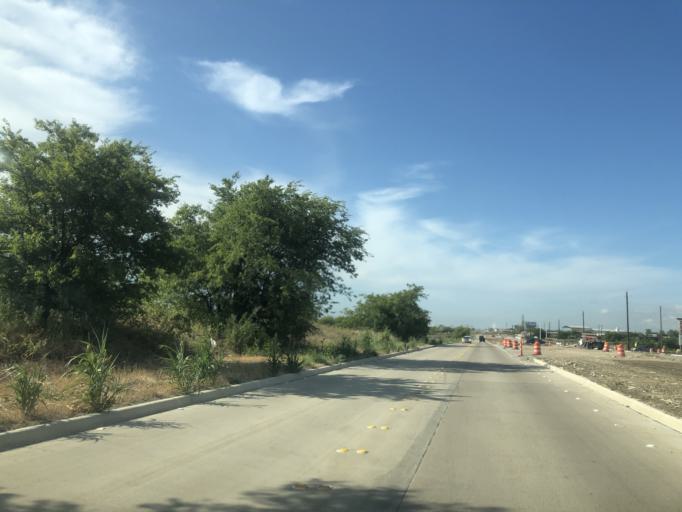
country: US
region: Texas
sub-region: Denton County
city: Justin
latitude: 33.0636
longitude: -97.2969
